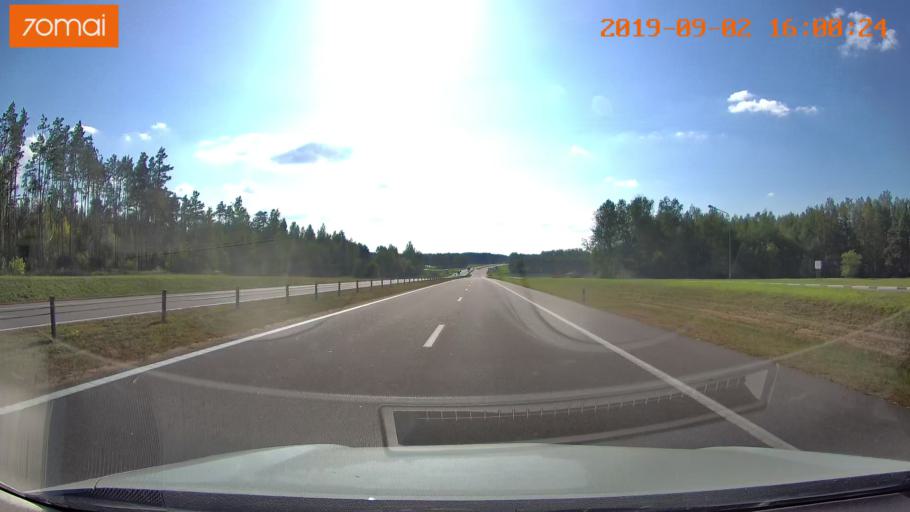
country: BY
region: Minsk
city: Byerazino
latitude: 53.8192
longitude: 28.9517
